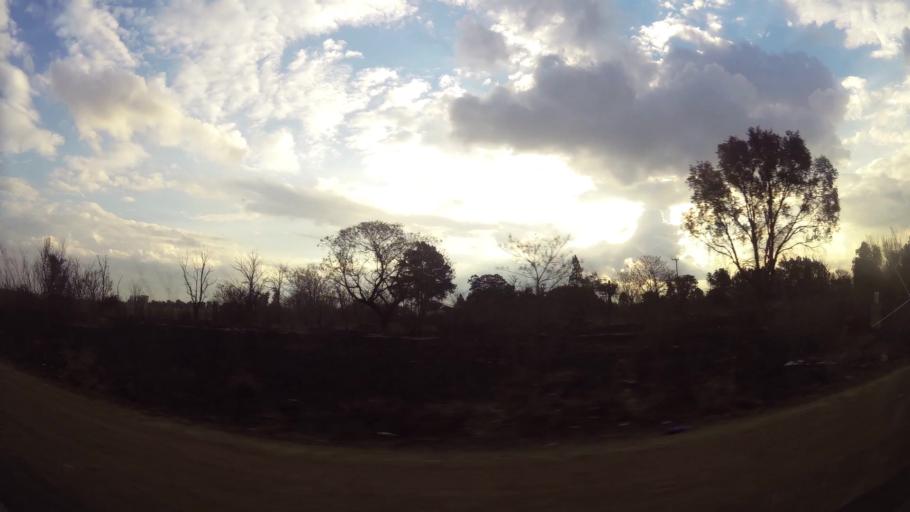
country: ZA
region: Gauteng
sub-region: Sedibeng District Municipality
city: Vanderbijlpark
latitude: -26.6452
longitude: 27.8043
